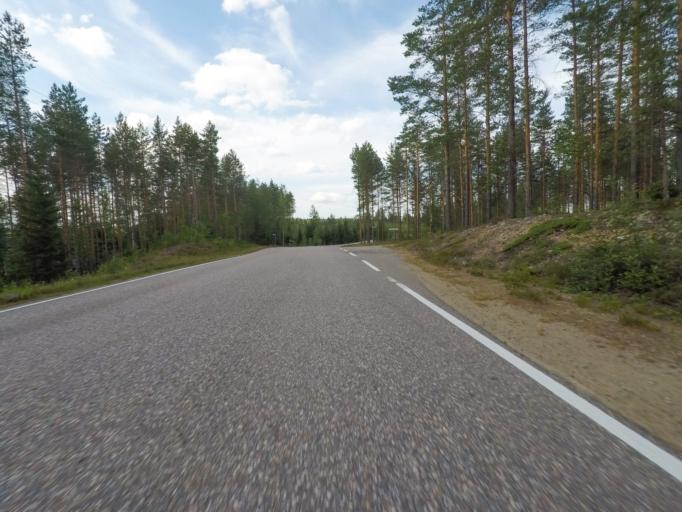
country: FI
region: Southern Savonia
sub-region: Savonlinna
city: Sulkava
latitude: 61.7404
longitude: 28.1980
